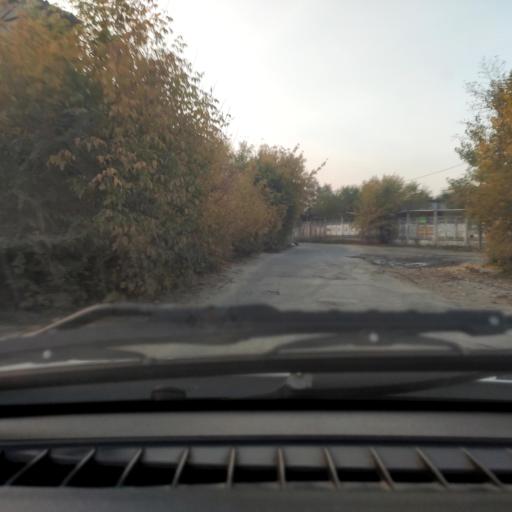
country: RU
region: Samara
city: Zhigulevsk
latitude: 53.4854
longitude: 49.4913
